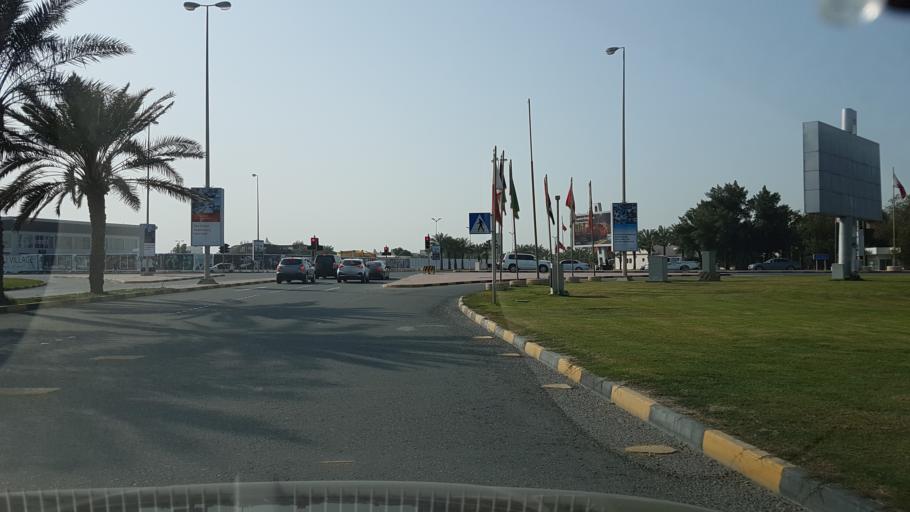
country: BH
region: Muharraq
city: Al Hadd
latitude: 26.2782
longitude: 50.6638
